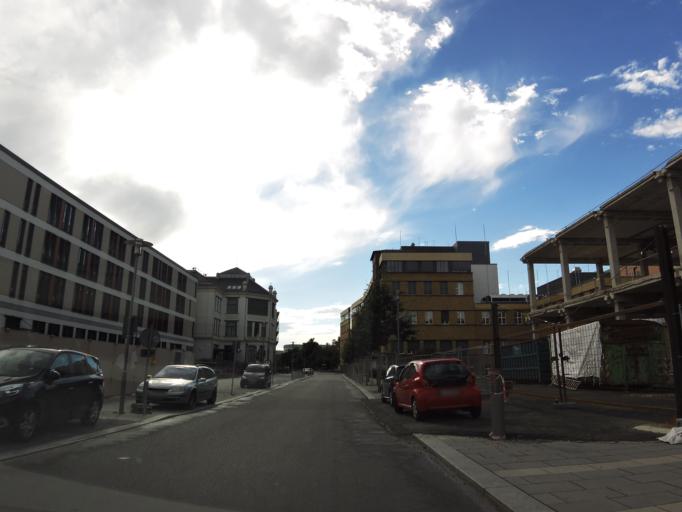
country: DE
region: Saxony
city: Leipzig
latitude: 51.3312
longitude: 12.3899
